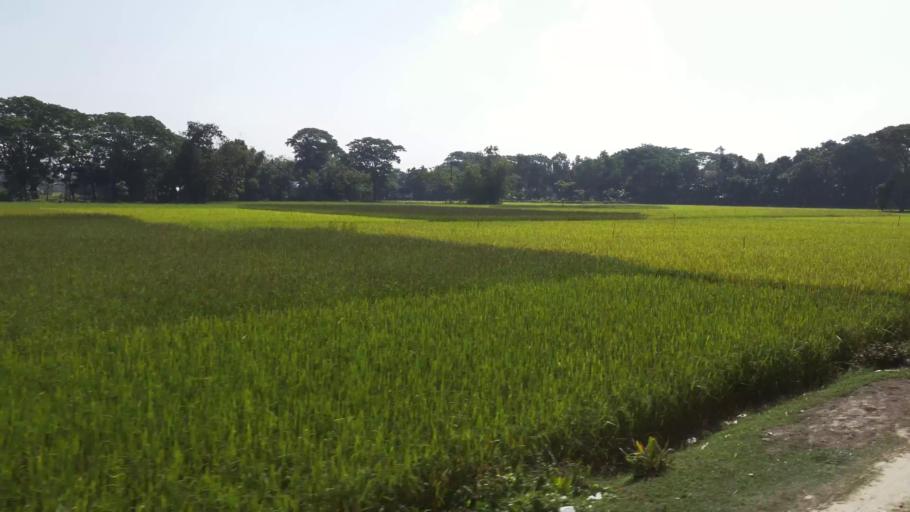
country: BD
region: Dhaka
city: Gafargaon
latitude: 24.4913
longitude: 90.5259
